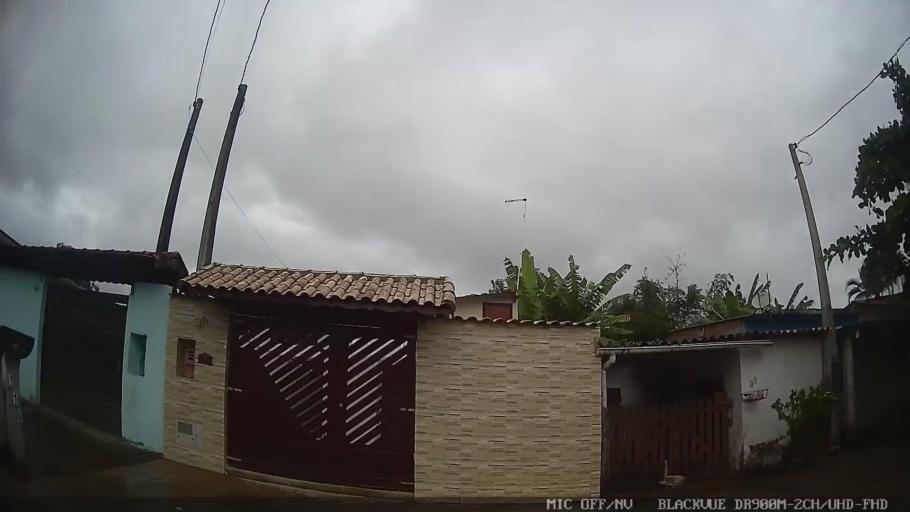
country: BR
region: Sao Paulo
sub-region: Itanhaem
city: Itanhaem
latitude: -24.1796
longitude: -46.8190
